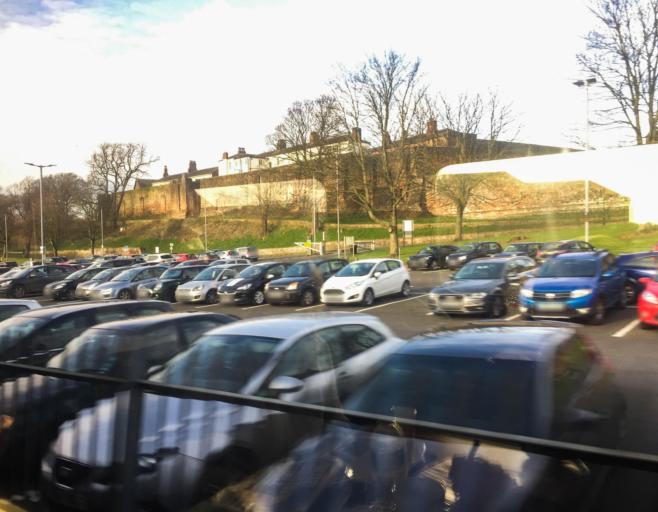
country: GB
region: England
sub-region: Cumbria
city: Carlisle
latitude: 54.8961
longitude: -2.9438
